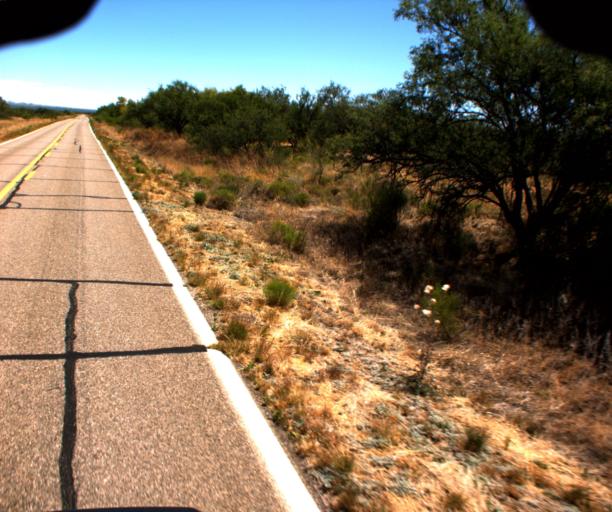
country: US
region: Arizona
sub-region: Pima County
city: Three Points
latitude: 31.7056
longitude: -111.4877
